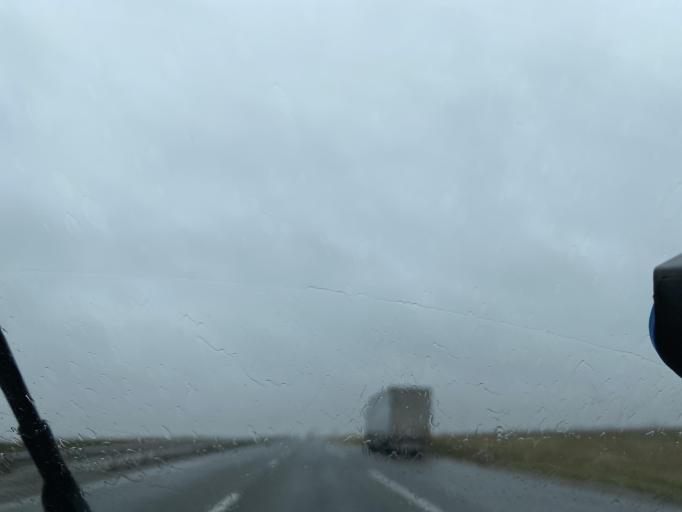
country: FR
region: Centre
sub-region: Departement d'Eure-et-Loir
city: Bailleau-l'Eveque
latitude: 48.5682
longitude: 1.4375
